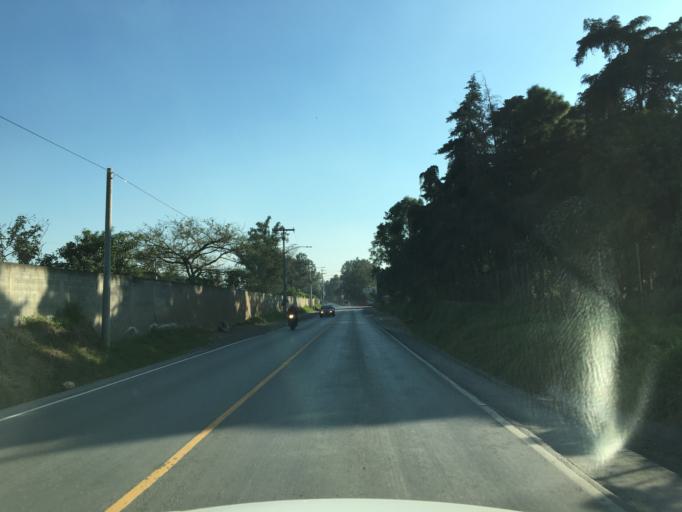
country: GT
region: Guatemala
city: Villa Nueva
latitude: 14.5285
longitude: -90.6169
